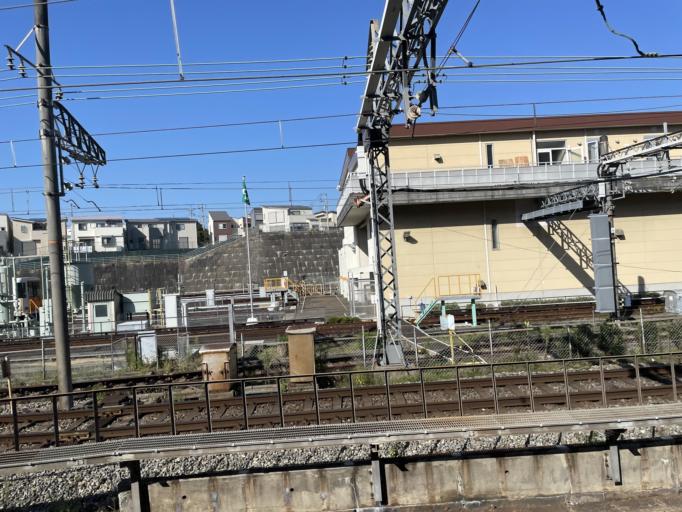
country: JP
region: Nara
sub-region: Ikoma-shi
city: Ikoma
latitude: 34.6914
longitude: 135.7120
